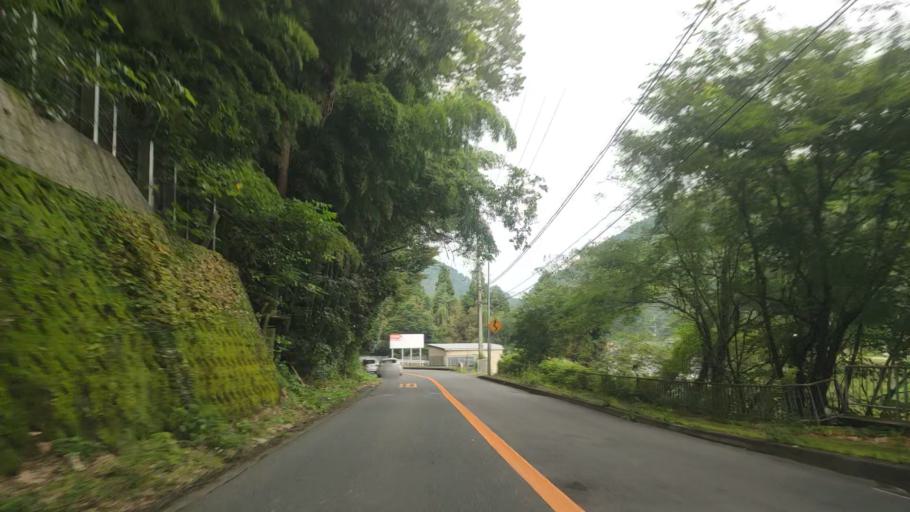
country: JP
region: Wakayama
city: Hashimoto
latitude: 34.3891
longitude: 135.6007
